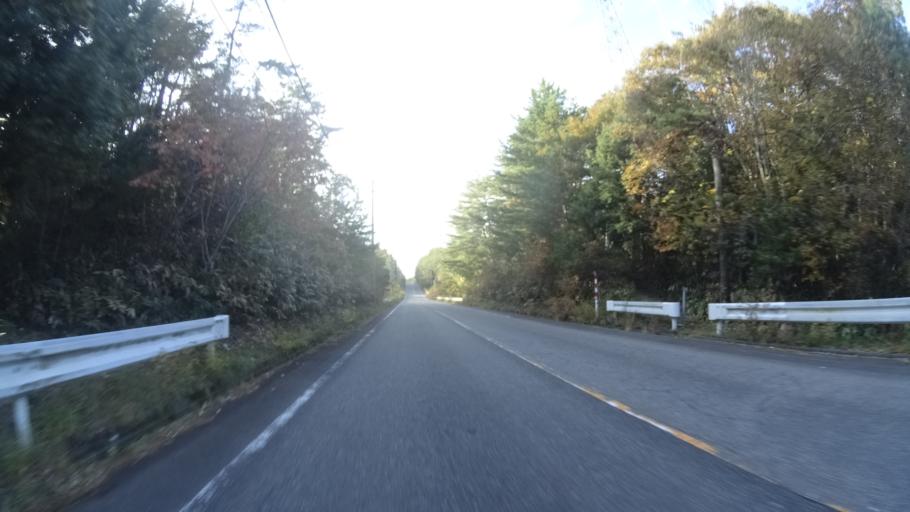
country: JP
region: Ishikawa
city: Hakui
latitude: 37.0688
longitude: 136.7495
